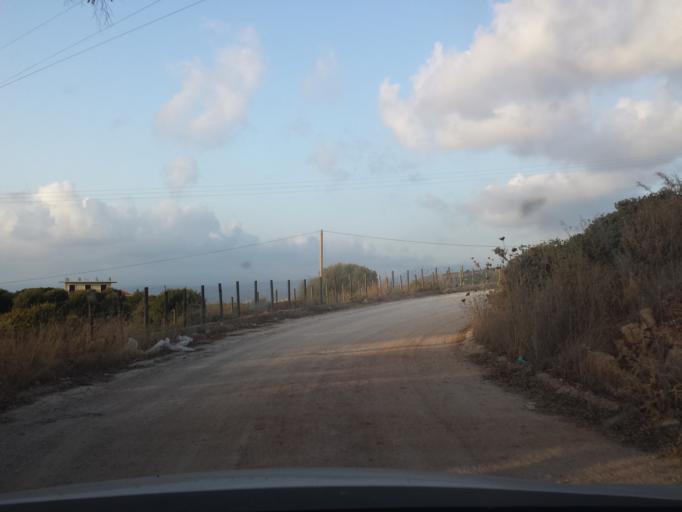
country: GR
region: Peloponnese
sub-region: Nomos Messinias
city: Pylos
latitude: 36.9019
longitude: 21.6941
